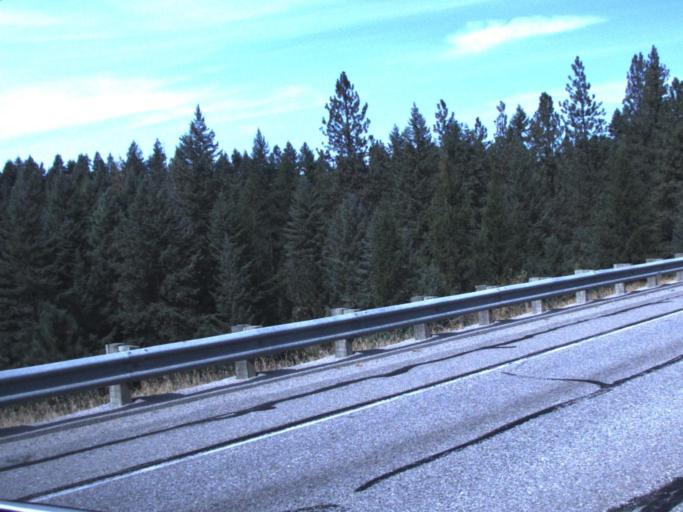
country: US
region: Washington
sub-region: Stevens County
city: Chewelah
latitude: 48.1320
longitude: -117.6544
